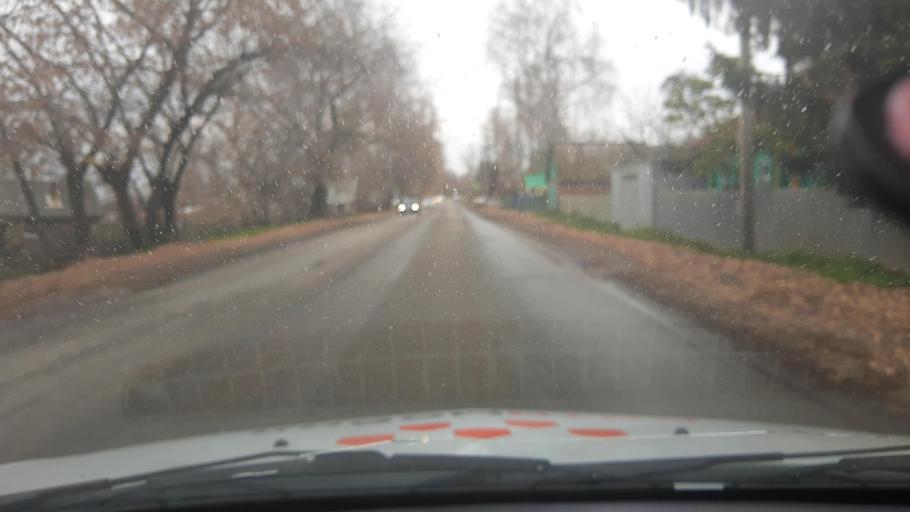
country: RU
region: Bashkortostan
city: Iglino
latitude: 54.7736
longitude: 56.2273
